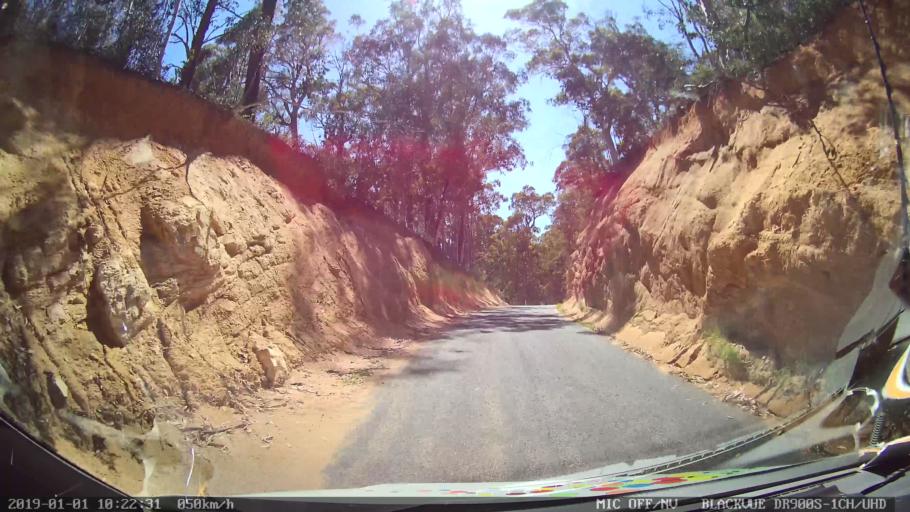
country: AU
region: New South Wales
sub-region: Snowy River
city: Jindabyne
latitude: -36.0775
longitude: 148.2045
